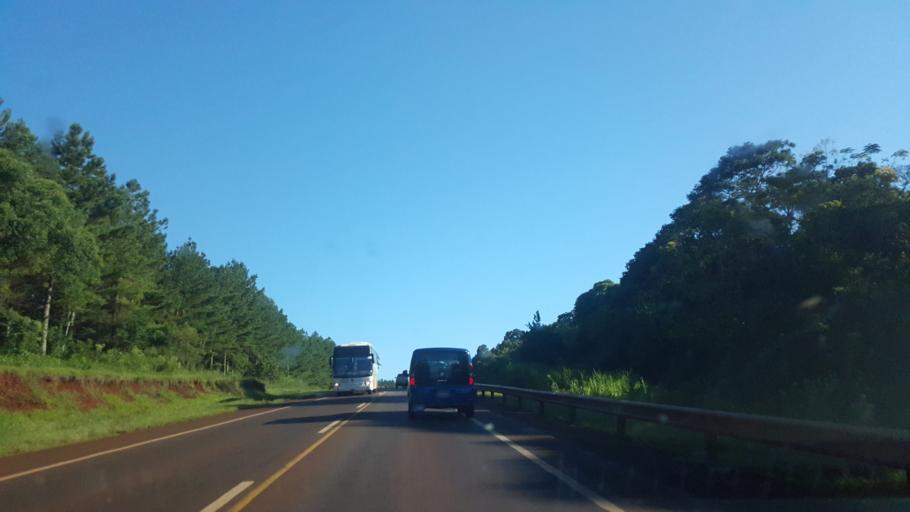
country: AR
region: Misiones
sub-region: Departamento de Eldorado
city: Eldorado
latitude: -26.2210
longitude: -54.5887
